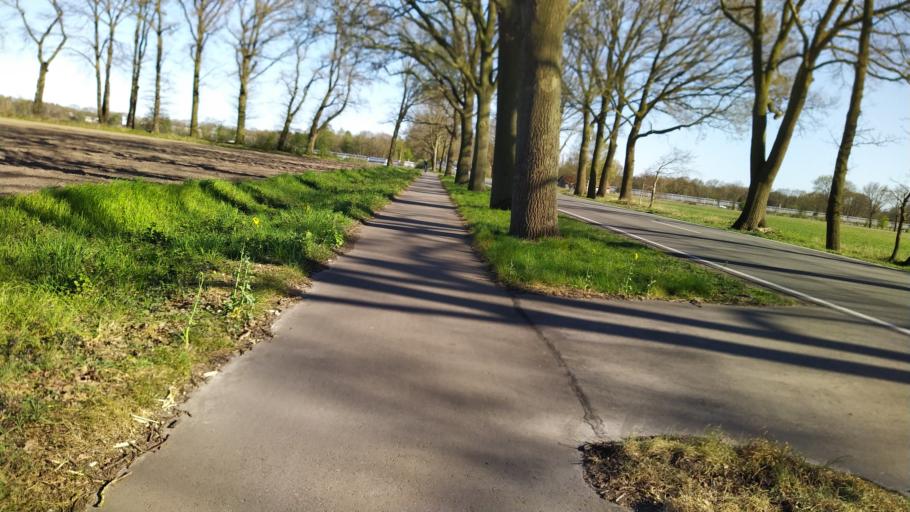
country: DE
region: Lower Saxony
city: Gross Meckelsen
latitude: 53.2850
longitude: 9.4704
